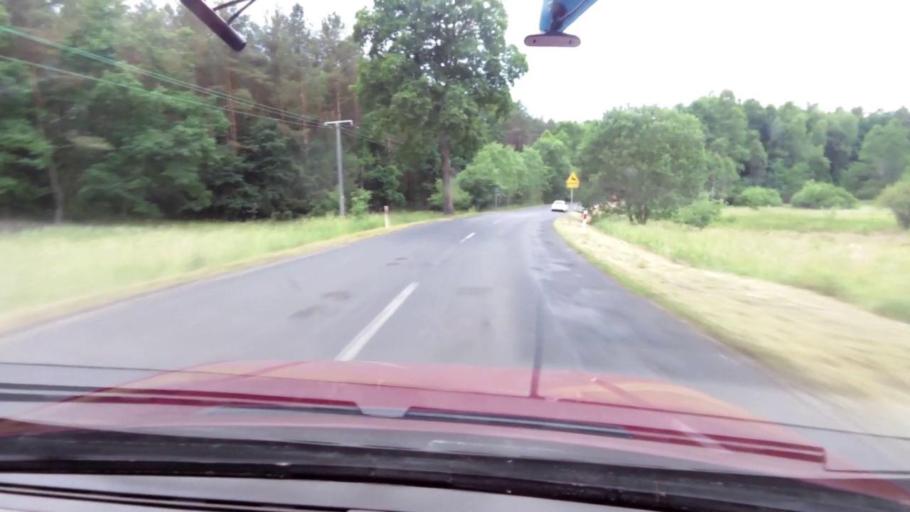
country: PL
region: West Pomeranian Voivodeship
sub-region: Powiat koszalinski
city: Sianow
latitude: 54.1775
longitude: 16.3650
